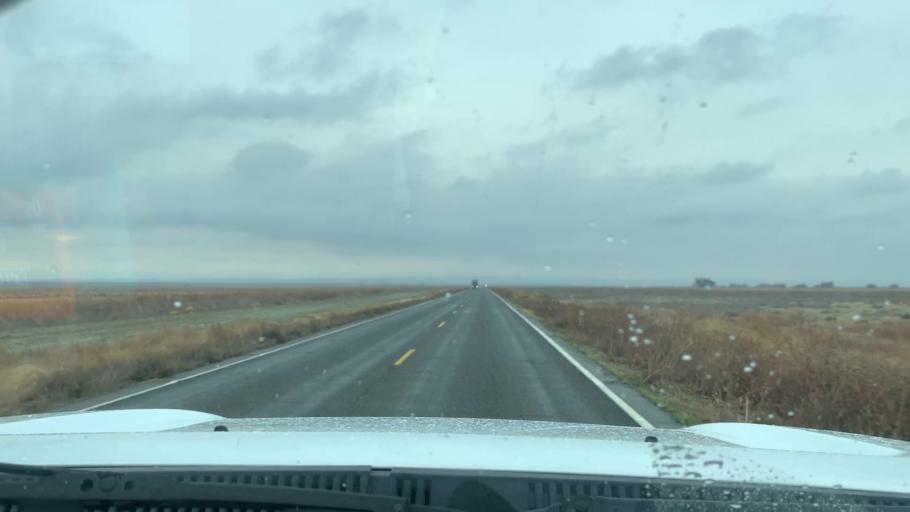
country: US
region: California
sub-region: Kings County
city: Kettleman City
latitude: 35.9341
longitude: -119.7926
